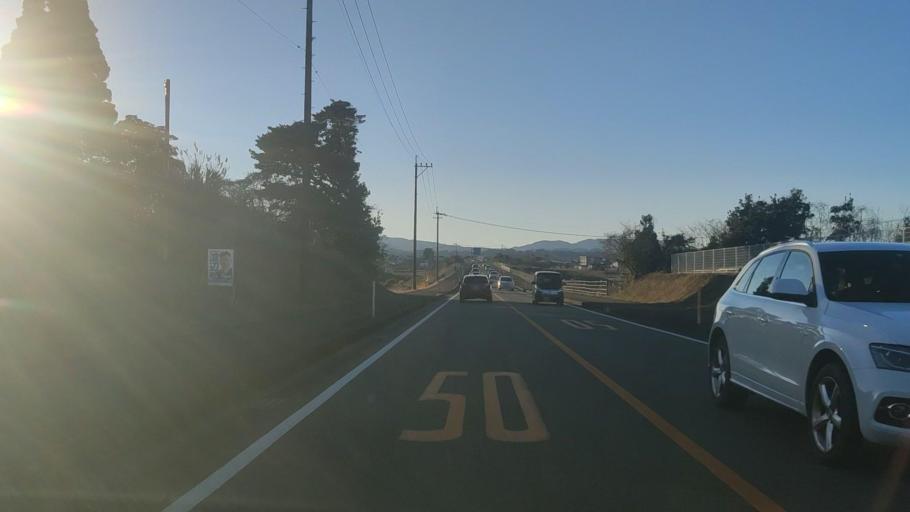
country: JP
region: Miyazaki
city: Miyazaki-shi
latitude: 31.8311
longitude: 131.3086
